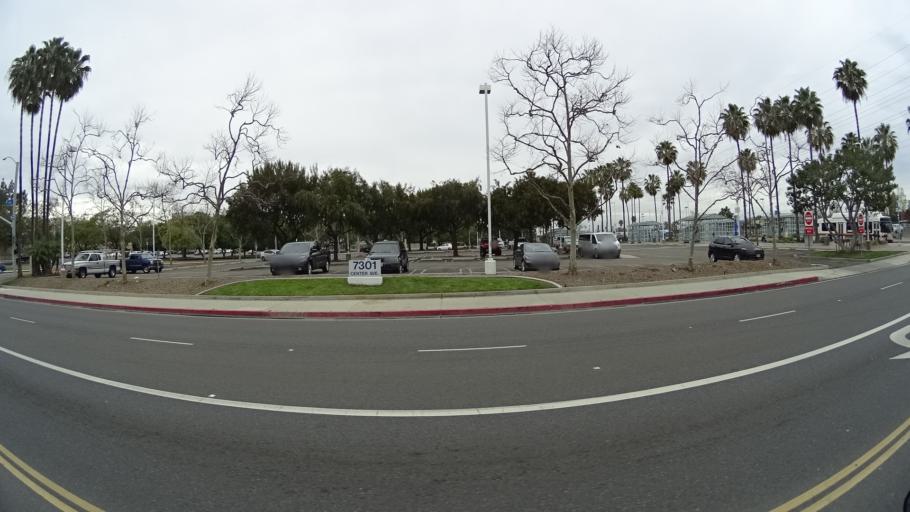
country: US
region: California
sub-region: Orange County
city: Midway City
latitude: 33.7338
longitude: -117.9999
